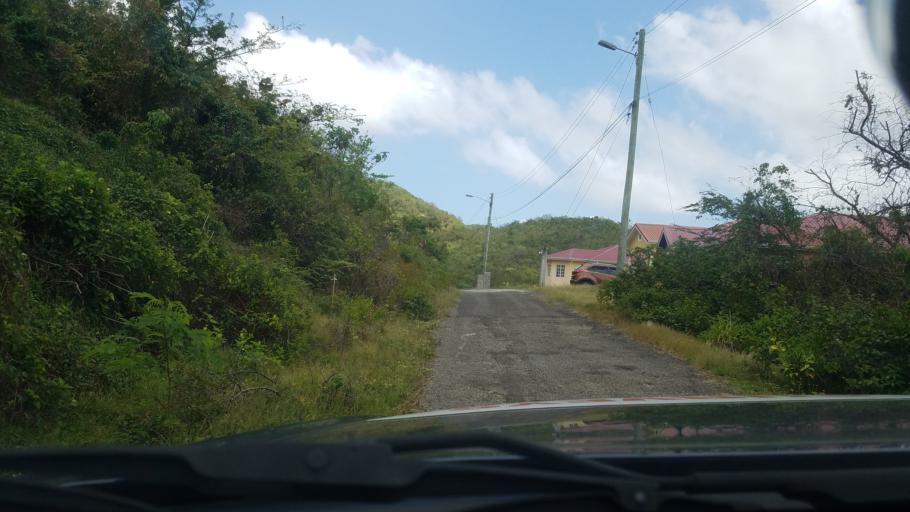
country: LC
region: Gros-Islet
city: Gros Islet
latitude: 14.0580
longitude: -60.9315
